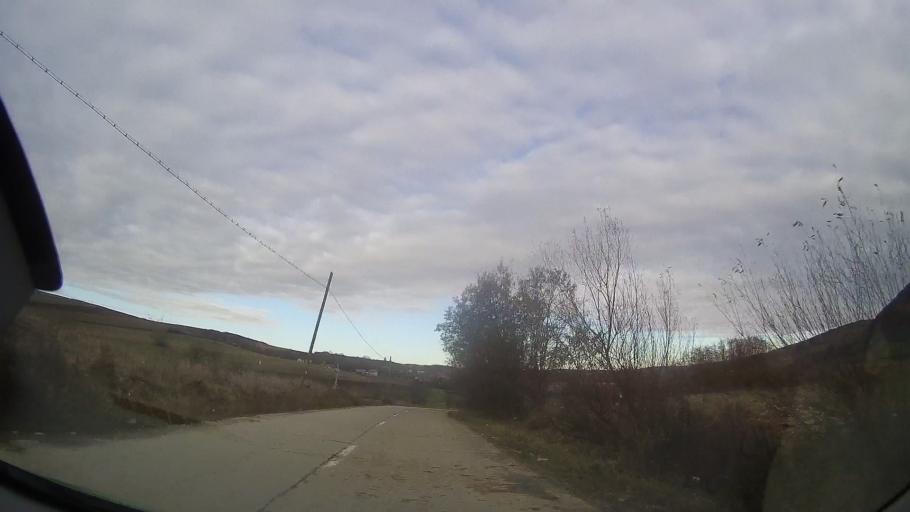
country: RO
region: Bistrita-Nasaud
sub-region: Comuna Sanmihaiu de Campie
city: Sanmihaiu de Campie
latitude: 46.8855
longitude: 24.3324
